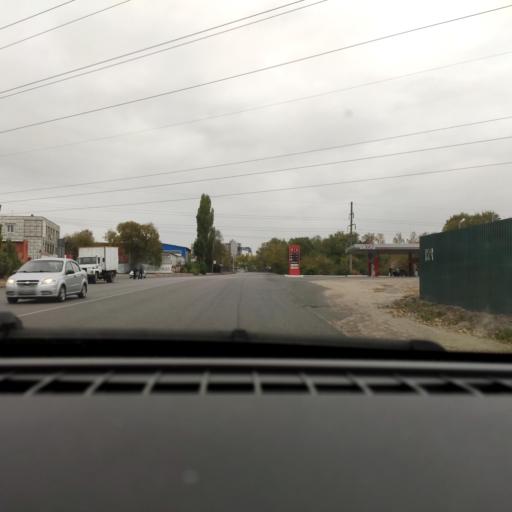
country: RU
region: Voronezj
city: Maslovka
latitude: 51.6276
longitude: 39.2618
